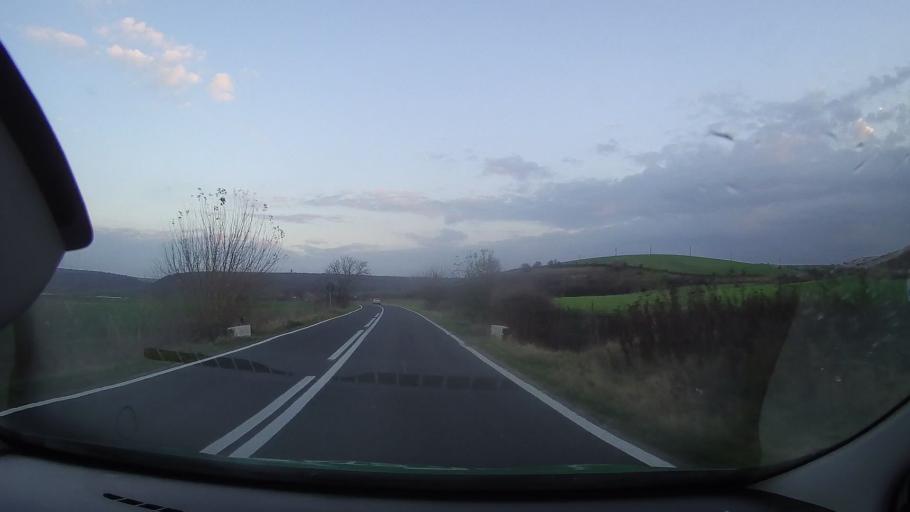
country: RO
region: Constanta
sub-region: Comuna Lipnita
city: Lipnita
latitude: 44.0981
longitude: 27.6310
